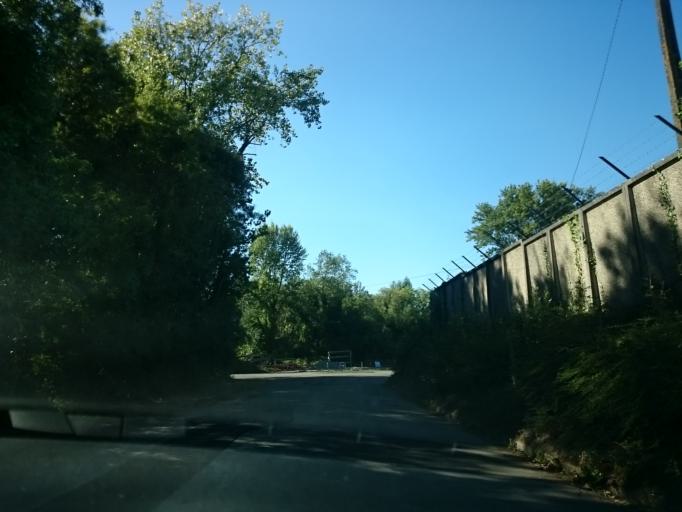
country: FR
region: Pays de la Loire
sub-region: Departement de la Loire-Atlantique
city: La Montagne
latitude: 47.1973
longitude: -1.6889
